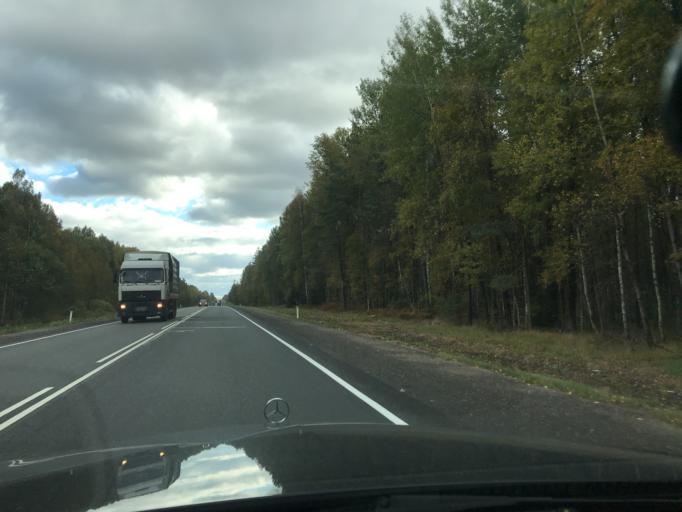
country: RU
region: Pskov
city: Opochka
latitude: 56.9583
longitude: 28.6370
